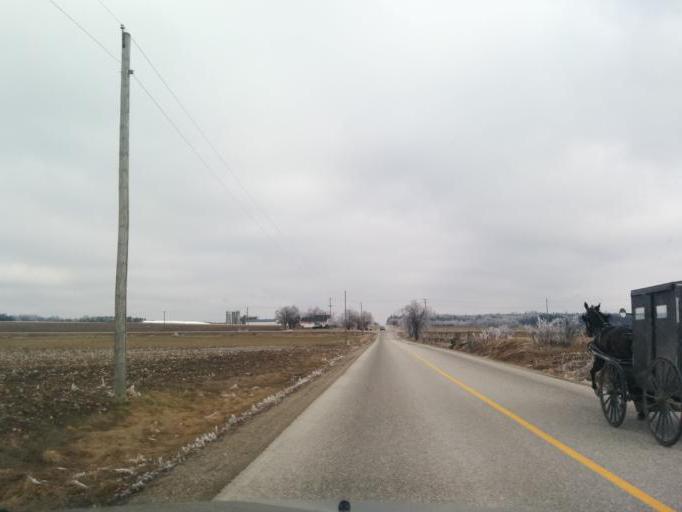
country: CA
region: Ontario
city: Waterloo
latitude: 43.6490
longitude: -80.5499
